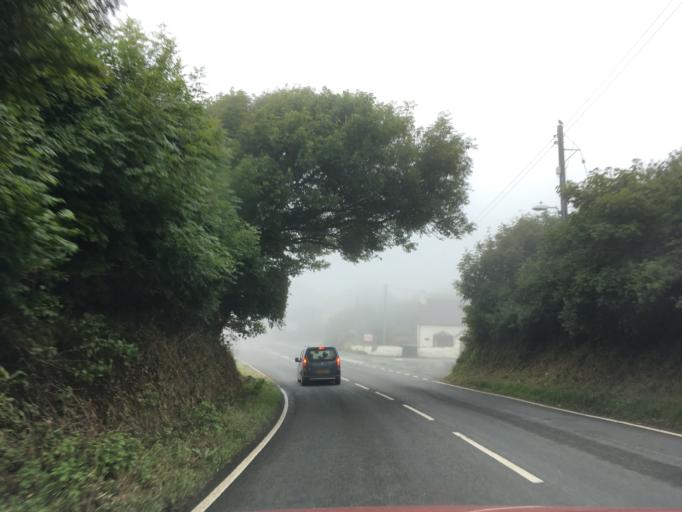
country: GB
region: Wales
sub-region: Pembrokeshire
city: Llanrhian
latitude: 51.8668
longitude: -5.1247
